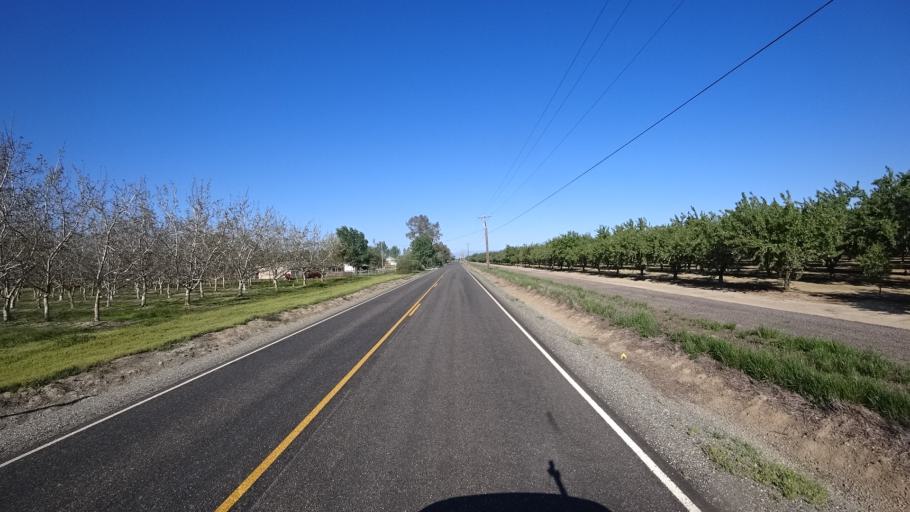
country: US
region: California
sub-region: Glenn County
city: Hamilton City
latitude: 39.7092
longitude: -122.0555
